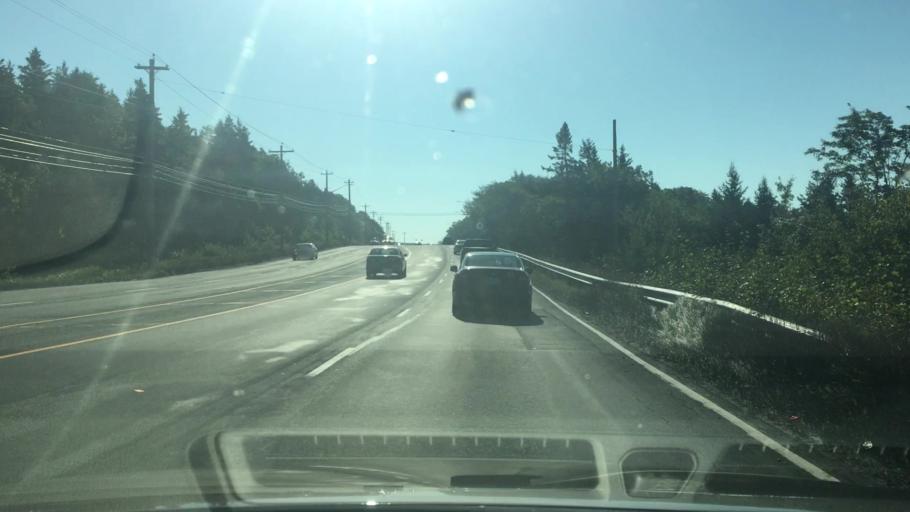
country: CA
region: Nova Scotia
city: Dartmouth
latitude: 44.7058
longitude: -63.6181
